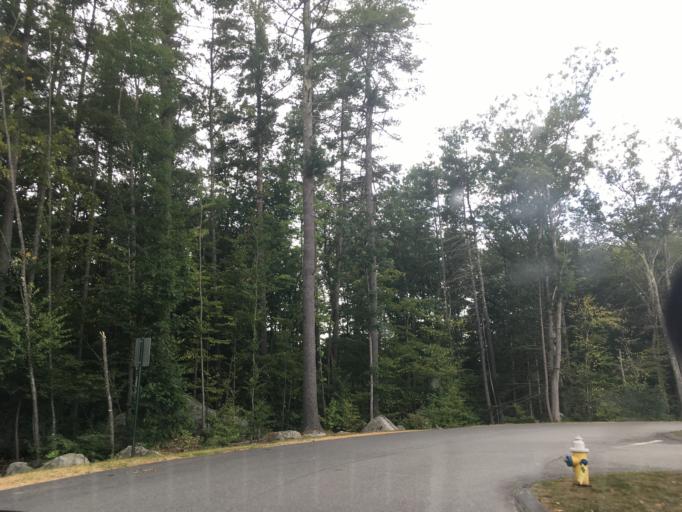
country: US
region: New Hampshire
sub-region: Rockingham County
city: Exeter
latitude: 42.9870
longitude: -70.9683
